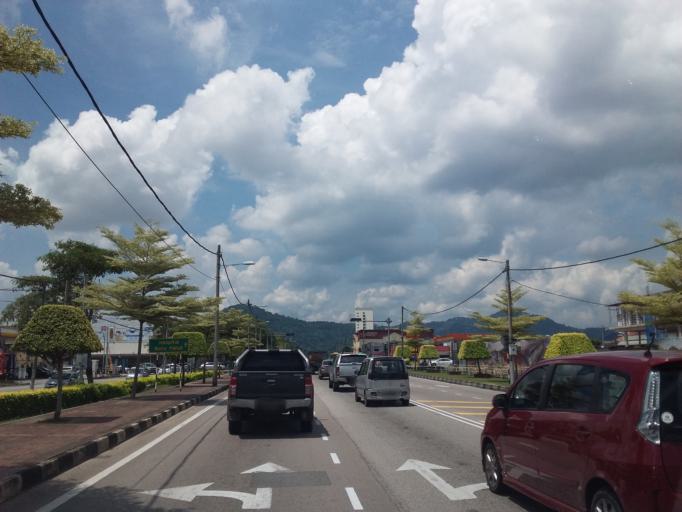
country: MY
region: Johor
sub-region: Daerah Batu Pahat
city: Batu Pahat
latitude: 1.8593
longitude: 102.9296
